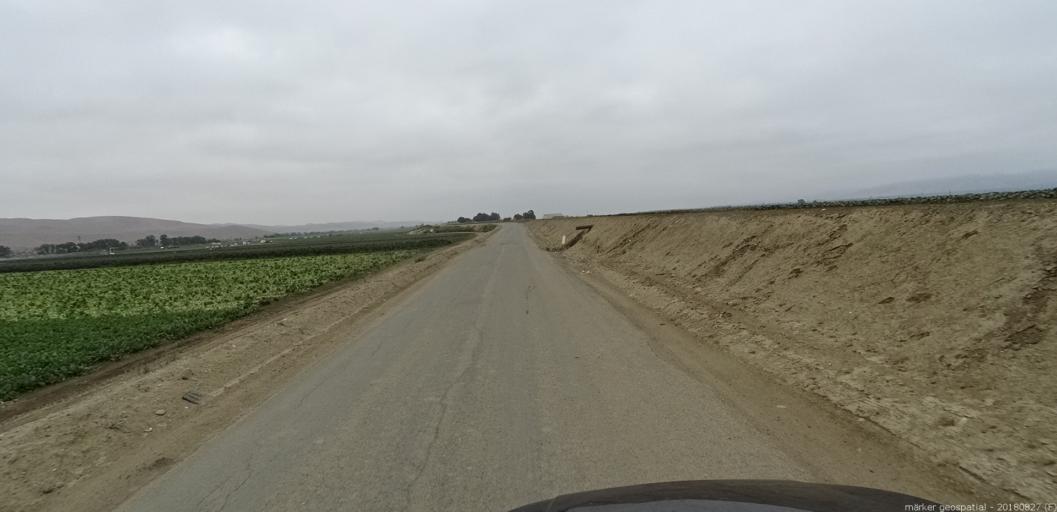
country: US
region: California
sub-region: Monterey County
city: Greenfield
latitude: 36.3313
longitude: -121.2108
